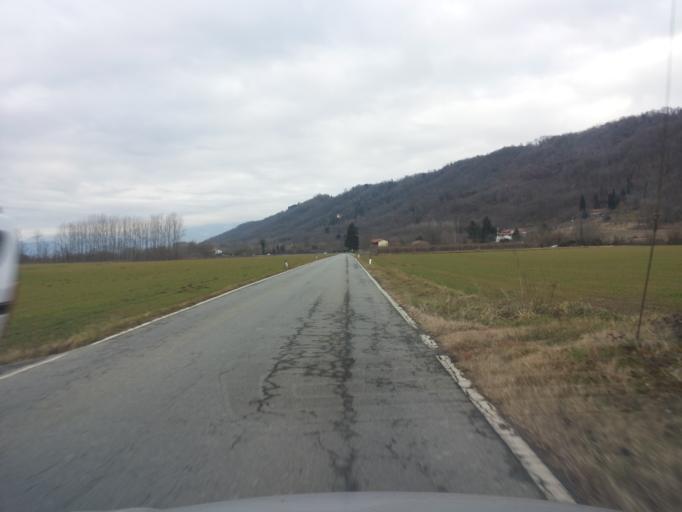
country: IT
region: Piedmont
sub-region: Provincia di Torino
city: Borgomasino
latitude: 45.3711
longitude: 7.9802
